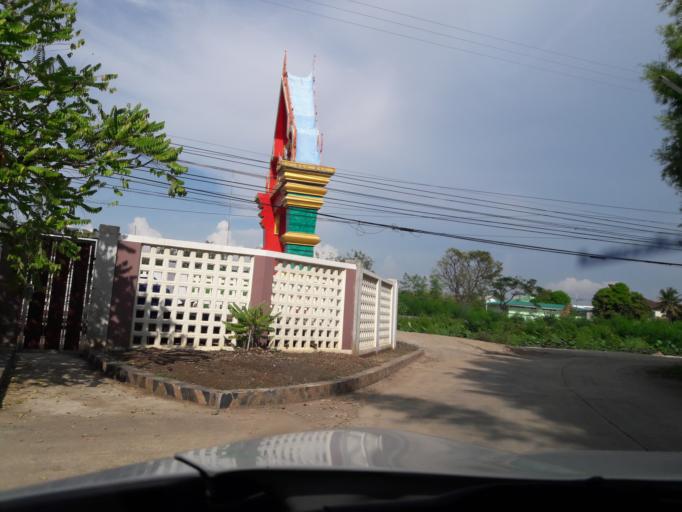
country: TH
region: Lop Buri
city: Ban Mi
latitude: 15.0437
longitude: 100.5358
